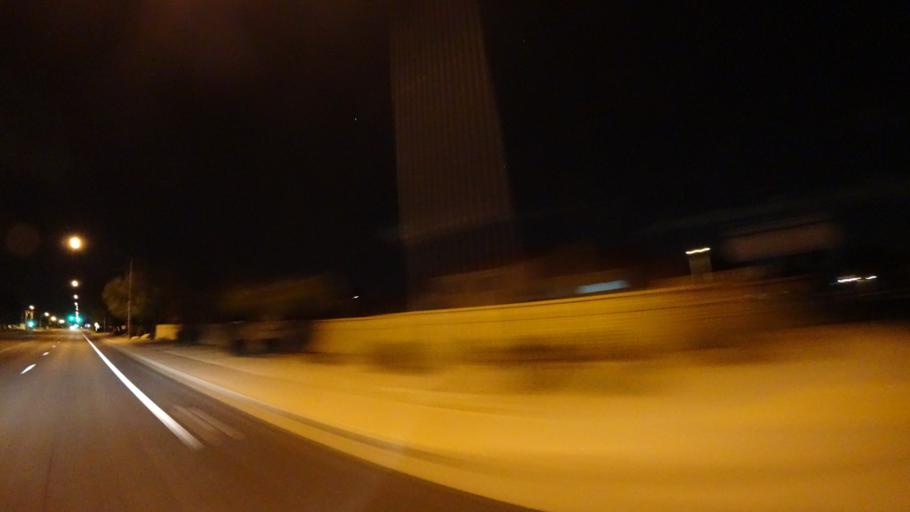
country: US
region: Arizona
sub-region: Maricopa County
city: Mesa
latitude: 33.4471
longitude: -111.7016
